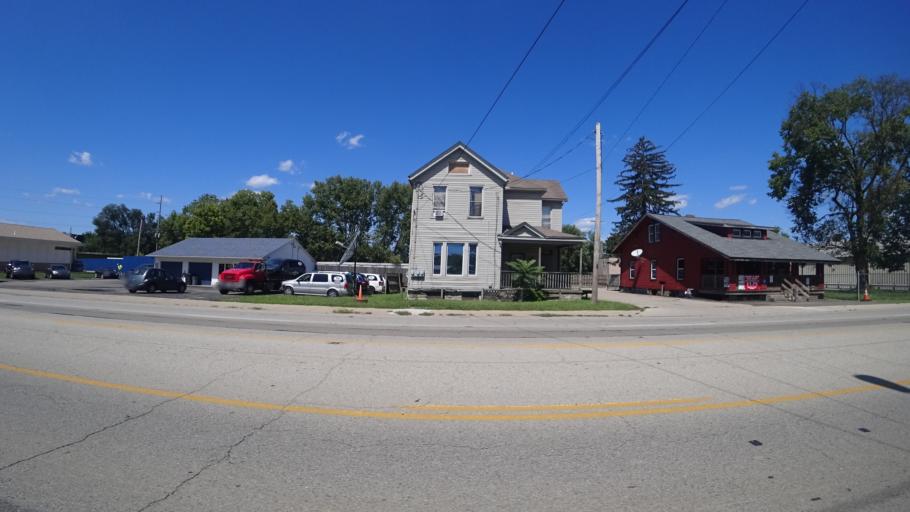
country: US
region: Ohio
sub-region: Butler County
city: Hamilton
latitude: 39.4033
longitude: -84.5334
